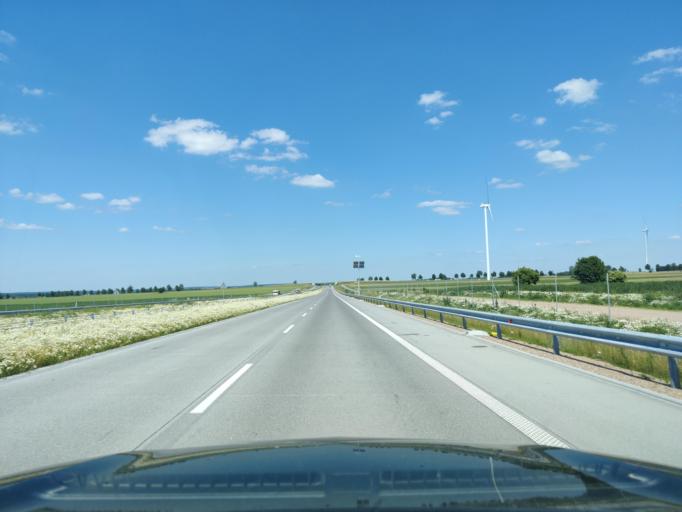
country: PL
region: Masovian Voivodeship
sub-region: Powiat mlawski
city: Wisniewo
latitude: 53.0509
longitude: 20.3616
